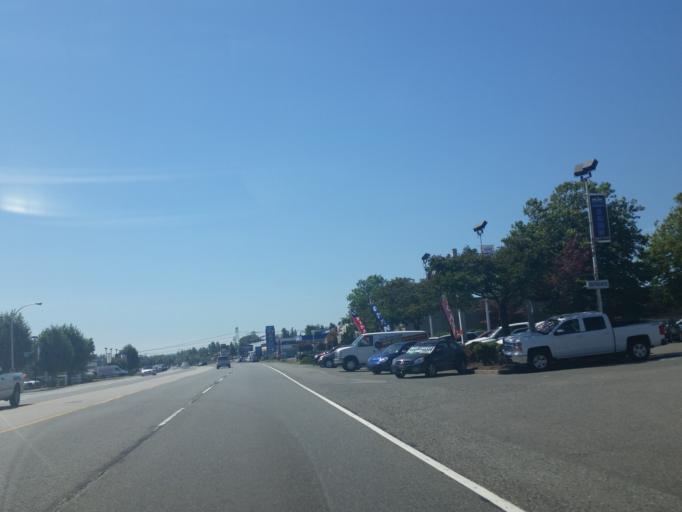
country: CA
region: British Columbia
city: Langley
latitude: 49.1083
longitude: -122.6834
